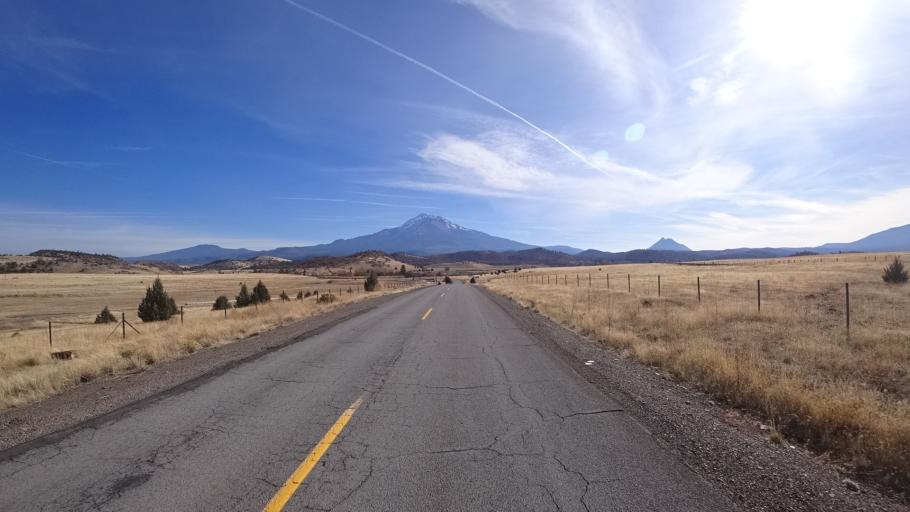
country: US
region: California
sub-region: Siskiyou County
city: Weed
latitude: 41.4719
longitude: -122.4473
